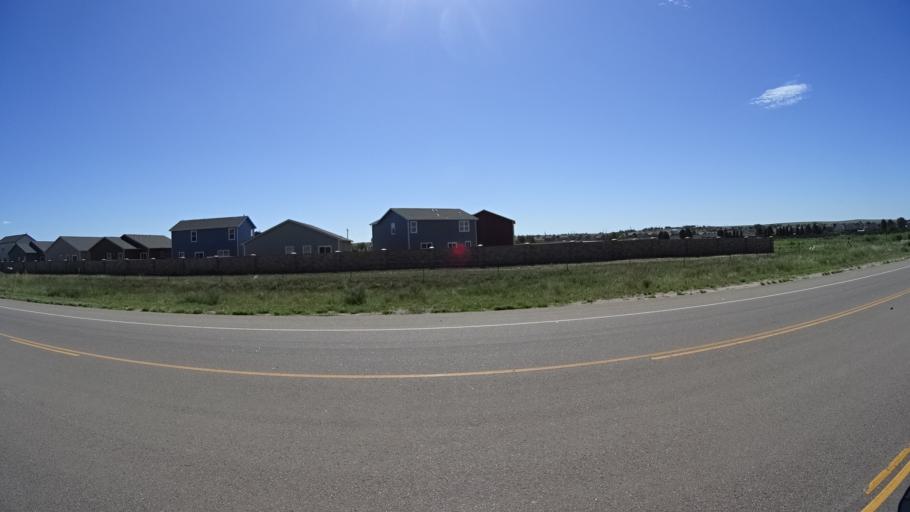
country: US
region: Colorado
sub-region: El Paso County
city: Security-Widefield
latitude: 38.7395
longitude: -104.6491
